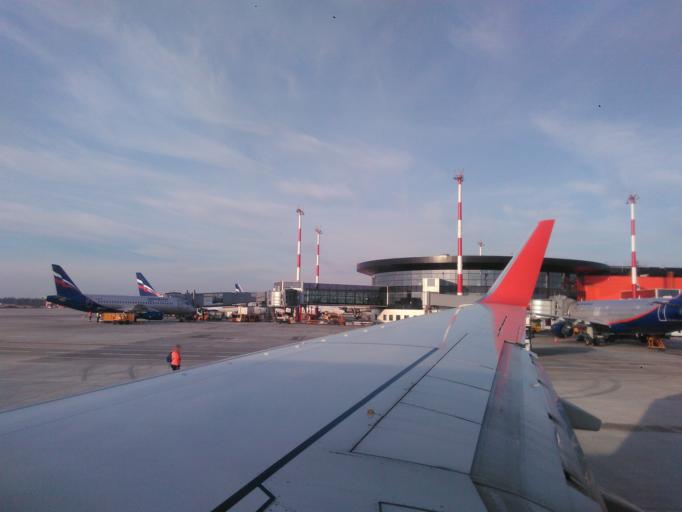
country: RU
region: Moskovskaya
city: Lobnya
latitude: 55.9786
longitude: 37.4203
